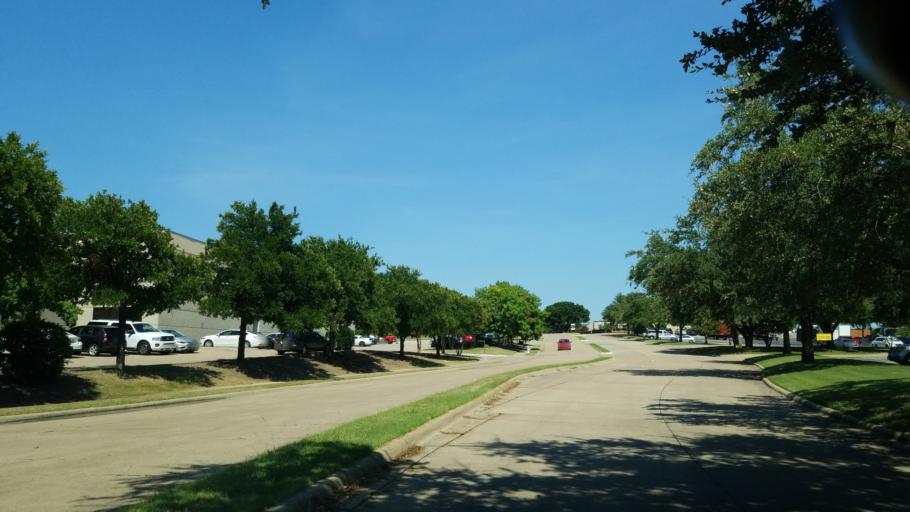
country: US
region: Texas
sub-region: Dallas County
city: Farmers Branch
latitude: 32.9146
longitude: -96.8912
